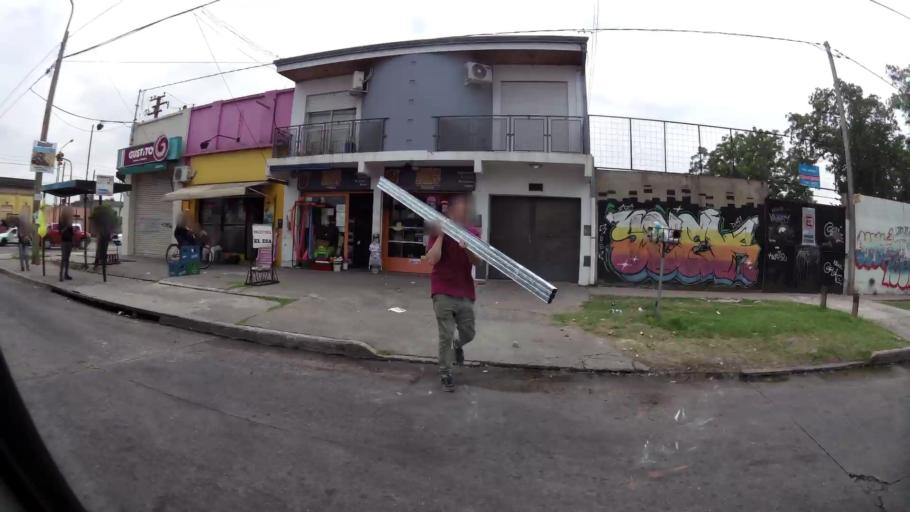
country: AR
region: Buenos Aires
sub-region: Partido de La Plata
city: La Plata
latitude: -34.8906
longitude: -57.9823
